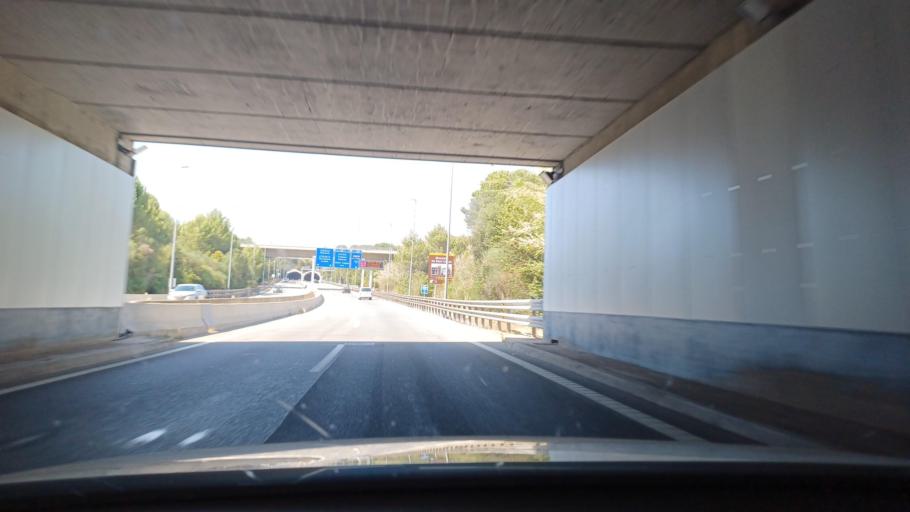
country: ES
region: Catalonia
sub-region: Provincia de Barcelona
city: Sant Cugat del Valles
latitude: 41.4688
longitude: 2.0648
